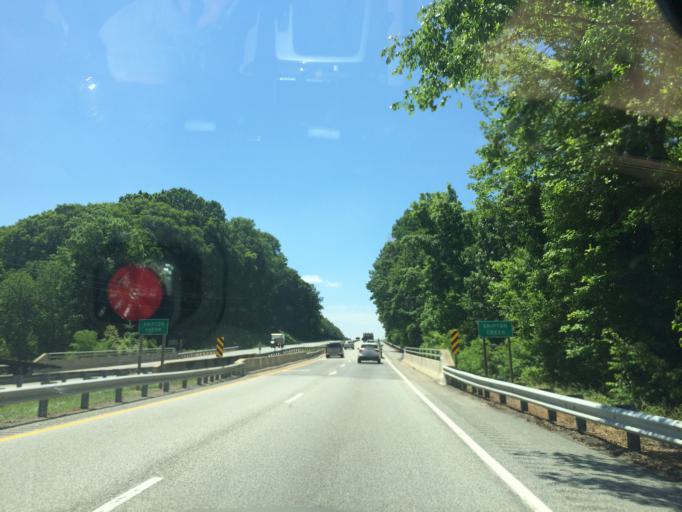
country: US
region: Maryland
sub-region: Talbot County
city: Easton
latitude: 38.8822
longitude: -76.0614
